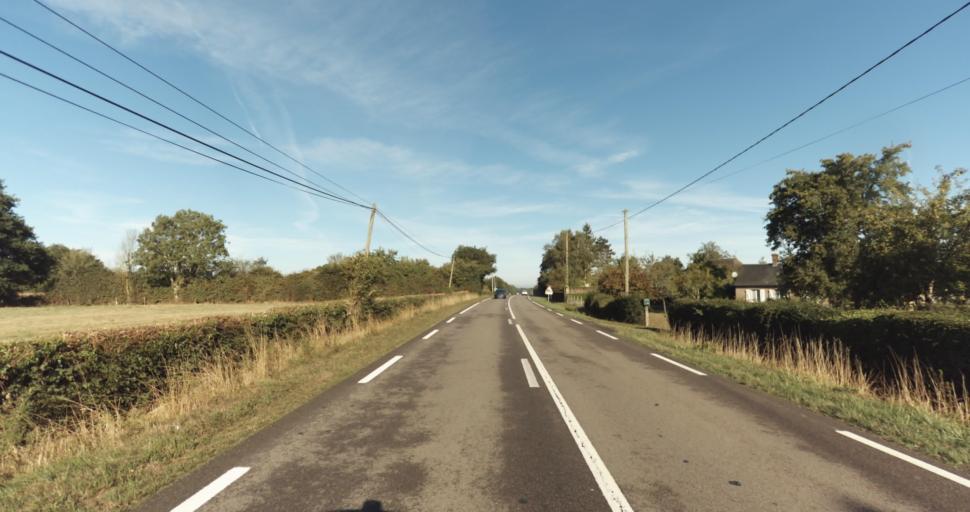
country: FR
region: Lower Normandy
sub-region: Departement de l'Orne
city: Vimoutiers
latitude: 48.9213
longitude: 0.2273
